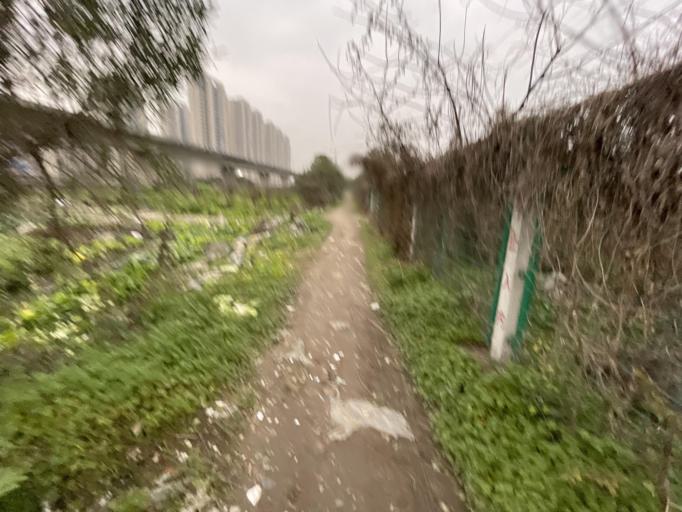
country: CN
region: Zhejiang Sheng
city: Louqiao
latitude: 27.9812
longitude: 120.6207
